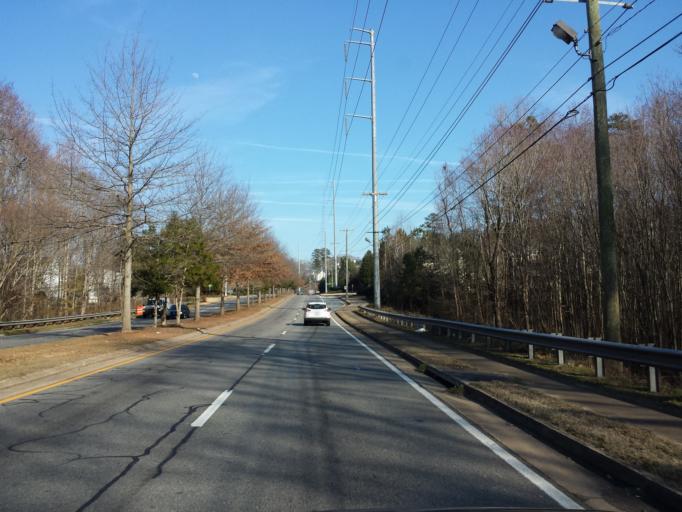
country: US
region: Georgia
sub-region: Cherokee County
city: Woodstock
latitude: 34.0356
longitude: -84.5386
